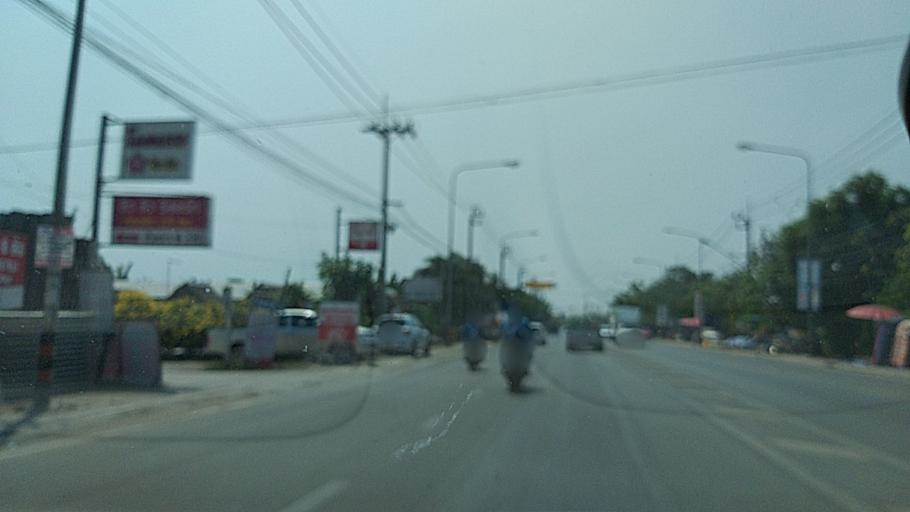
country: TH
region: Nonthaburi
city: Bang Bua Thong
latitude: 13.9097
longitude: 100.3598
